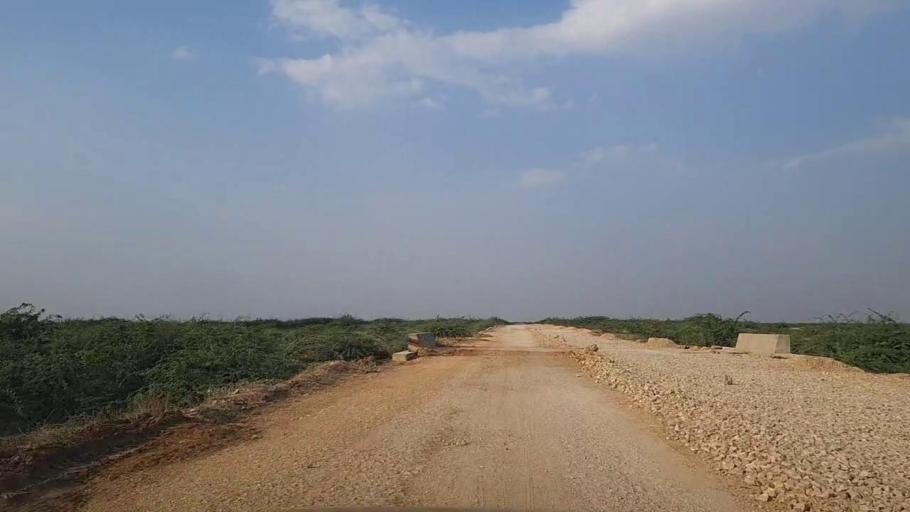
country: PK
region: Sindh
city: Gharo
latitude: 24.8357
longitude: 67.7456
